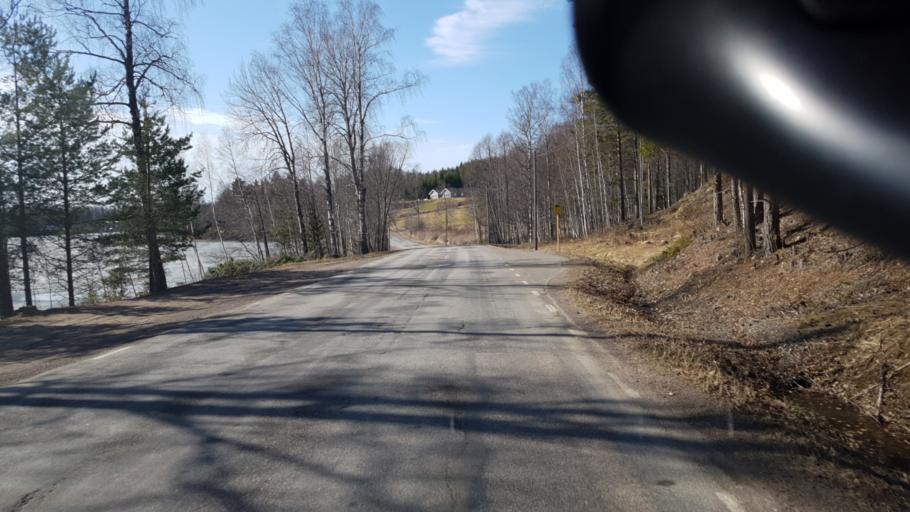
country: SE
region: Vaermland
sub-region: Arvika Kommun
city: Arvika
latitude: 59.6626
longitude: 12.6963
